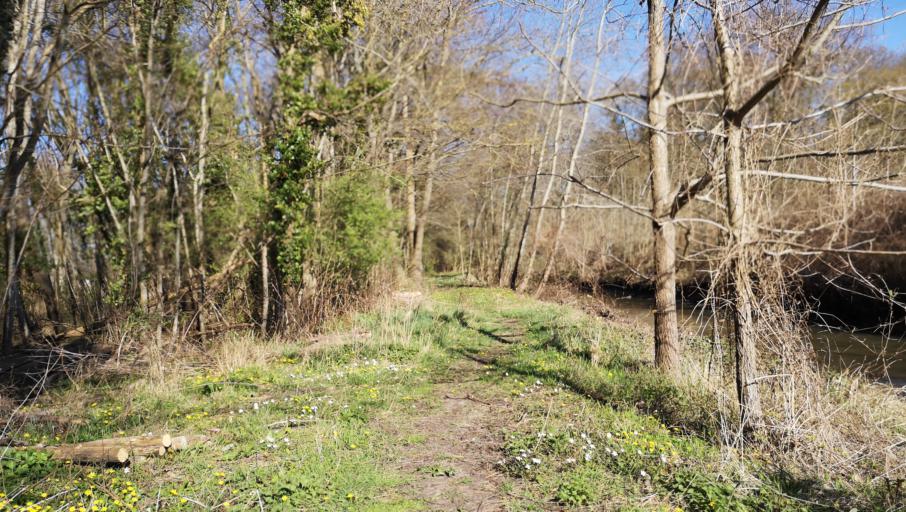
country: FR
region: Centre
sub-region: Departement du Loiret
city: Saint-Jean-de-Braye
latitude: 47.9037
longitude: 1.9884
